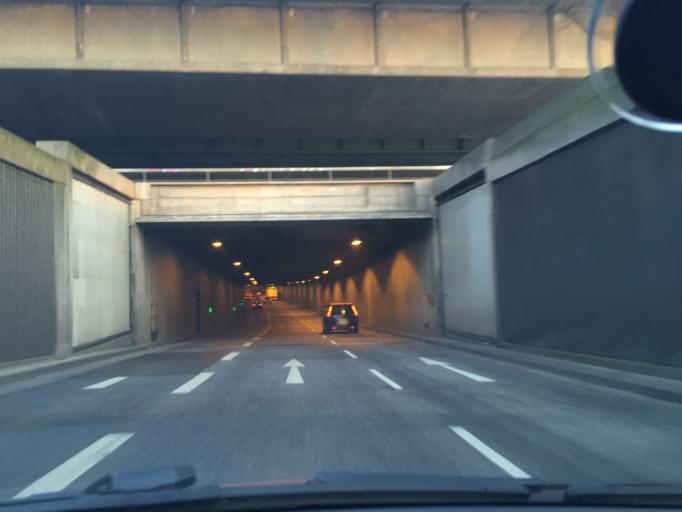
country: DE
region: North Rhine-Westphalia
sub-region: Regierungsbezirk Koln
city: Altstadt Sud
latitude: 50.9359
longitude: 6.9632
